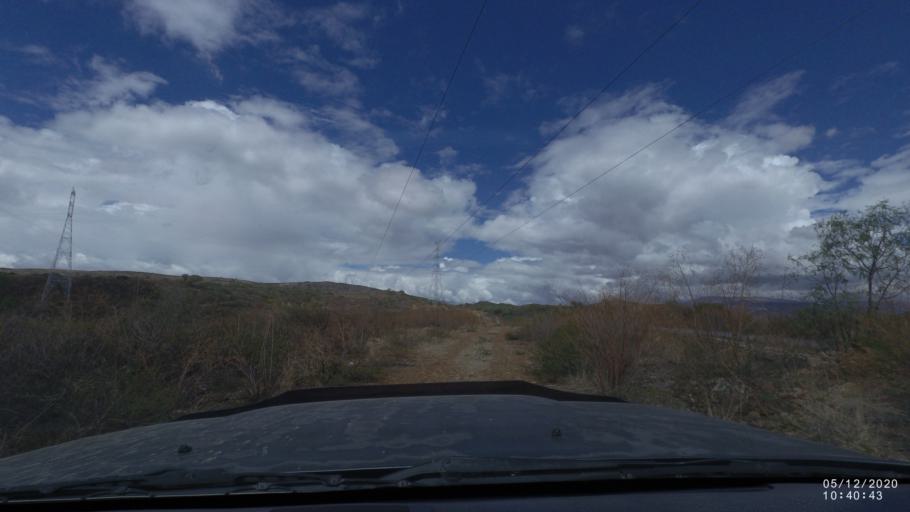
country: BO
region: Cochabamba
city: Sipe Sipe
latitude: -17.5456
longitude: -66.2882
